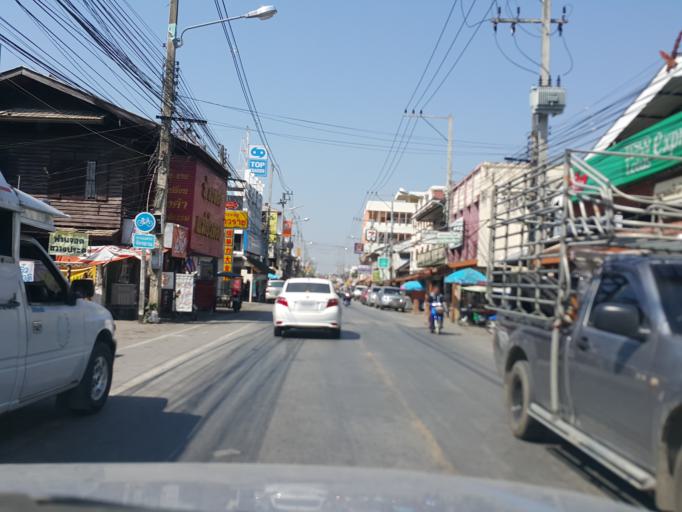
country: TH
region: Chiang Mai
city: San Kamphaeng
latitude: 18.7426
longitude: 99.1227
